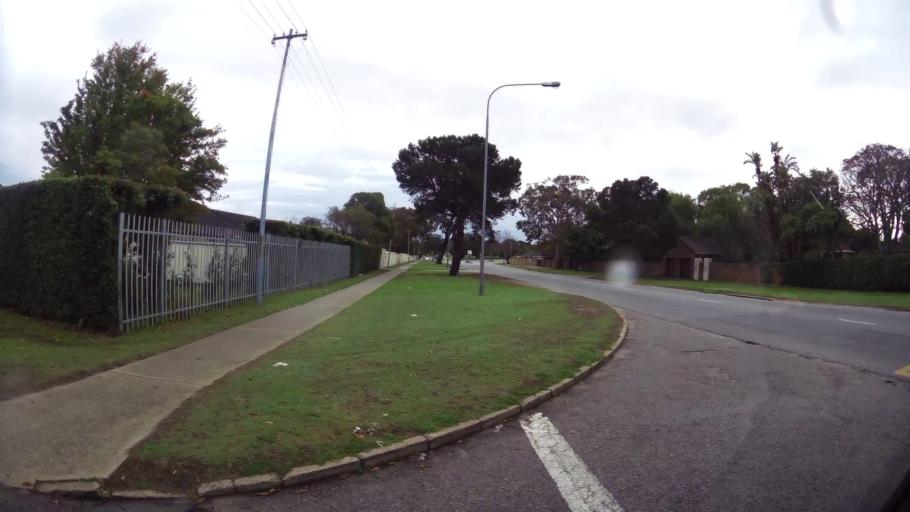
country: ZA
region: Eastern Cape
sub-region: Nelson Mandela Bay Metropolitan Municipality
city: Port Elizabeth
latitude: -33.9766
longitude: 25.5856
